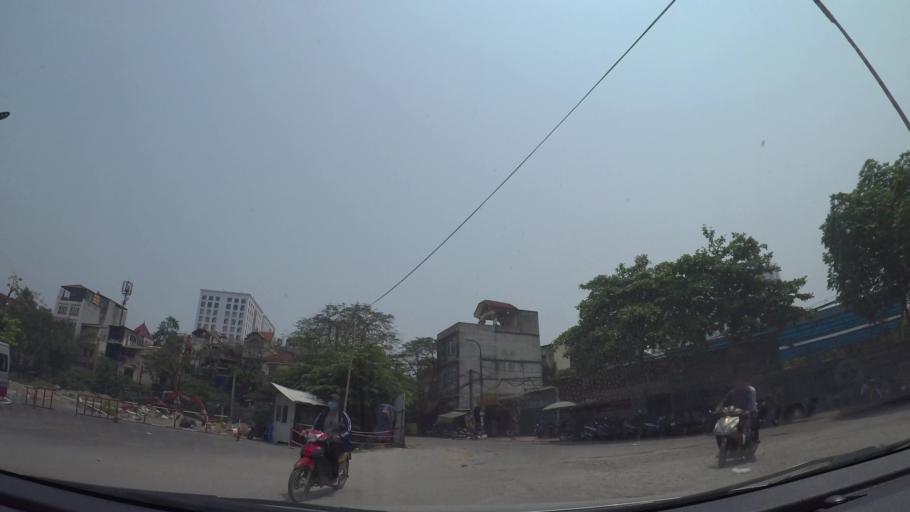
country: VN
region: Ha Noi
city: Thanh Xuan
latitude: 20.9979
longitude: 105.7872
